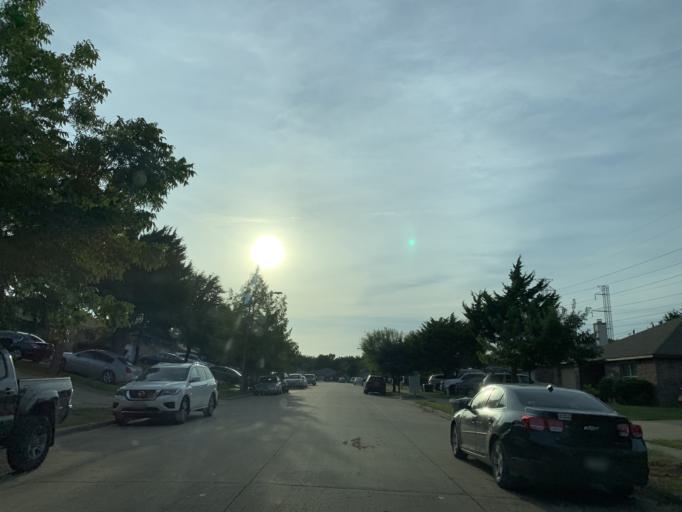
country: US
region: Texas
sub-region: Dallas County
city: Cockrell Hill
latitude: 32.7075
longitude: -96.9030
